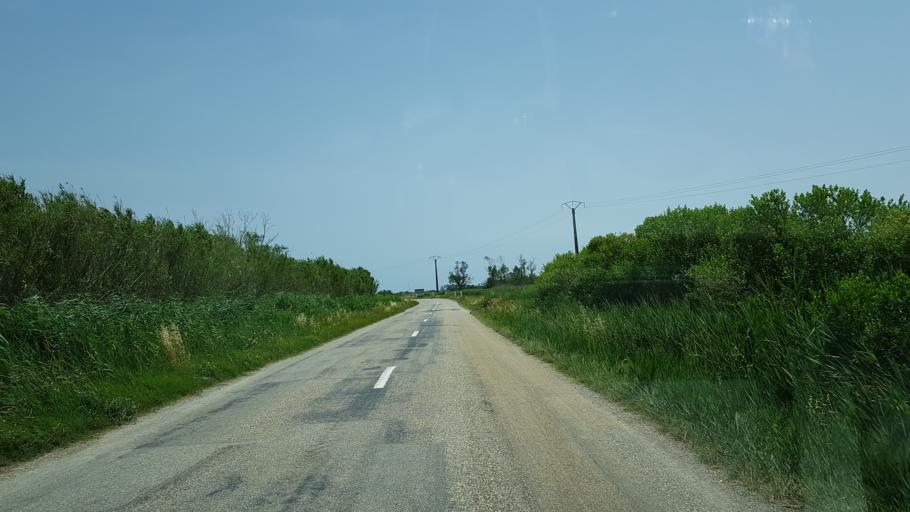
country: FR
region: Provence-Alpes-Cote d'Azur
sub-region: Departement des Bouches-du-Rhone
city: Port-Saint-Louis-du-Rhone
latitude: 43.4453
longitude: 4.6661
